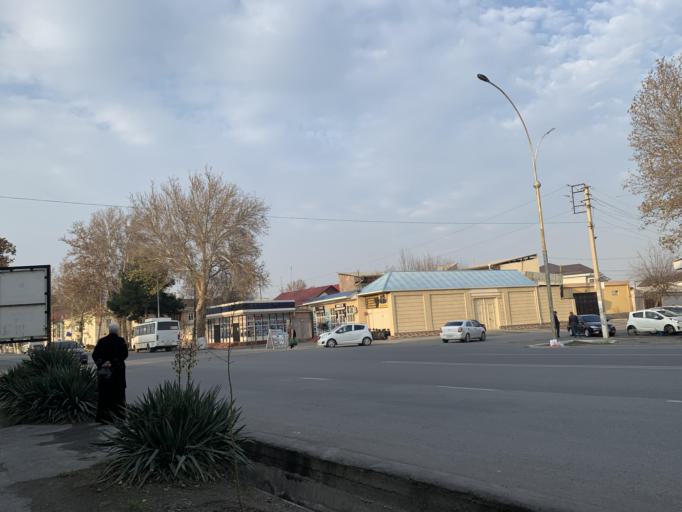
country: UZ
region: Fergana
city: Qo`qon
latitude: 40.5391
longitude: 70.9241
